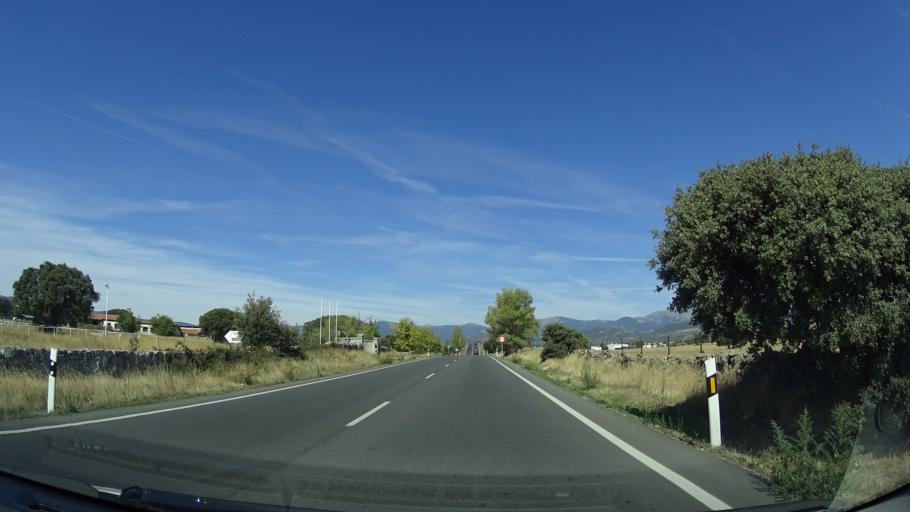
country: ES
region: Madrid
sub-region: Provincia de Madrid
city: Collado-Villalba
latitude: 40.6169
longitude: -4.0246
